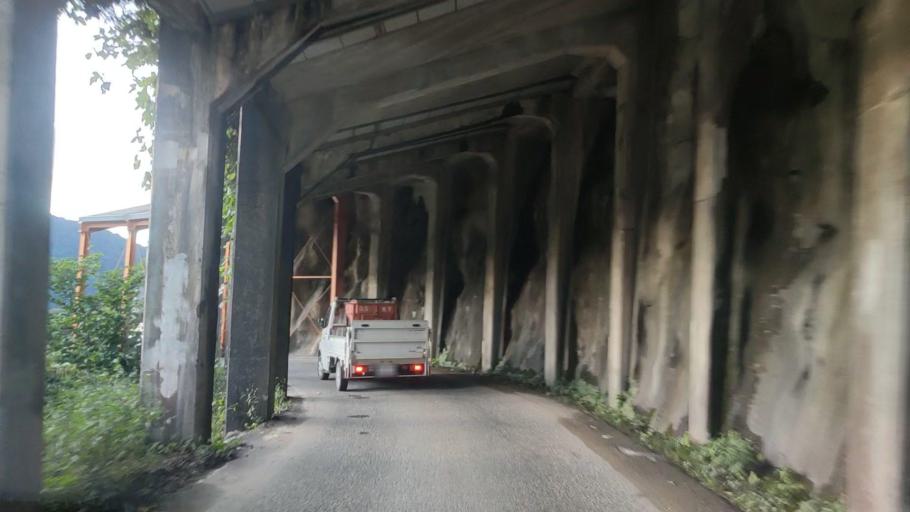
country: JP
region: Toyama
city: Nanto-shi
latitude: 36.5401
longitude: 137.0109
